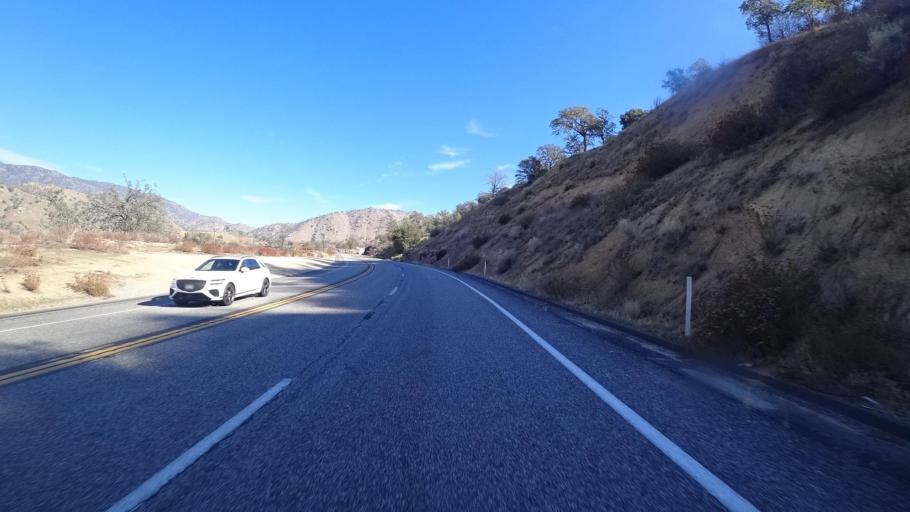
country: US
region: California
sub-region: Kern County
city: Bodfish
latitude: 35.5309
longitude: -118.6351
